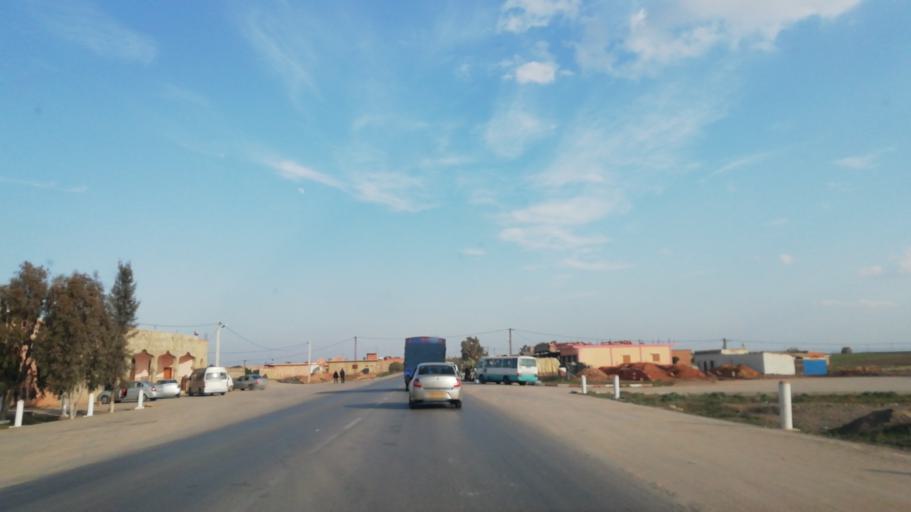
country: DZ
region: Relizane
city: Relizane
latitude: 35.8980
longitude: 0.5862
